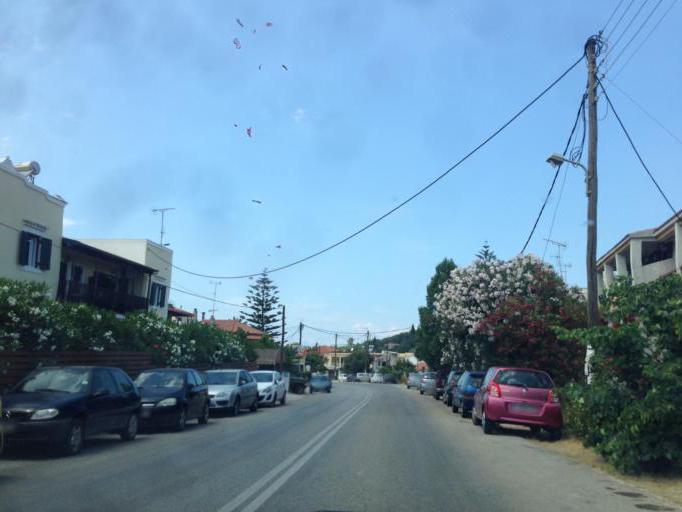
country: GR
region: Ionian Islands
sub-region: Nomos Kerkyras
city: Acharavi
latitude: 39.7868
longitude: 19.9201
